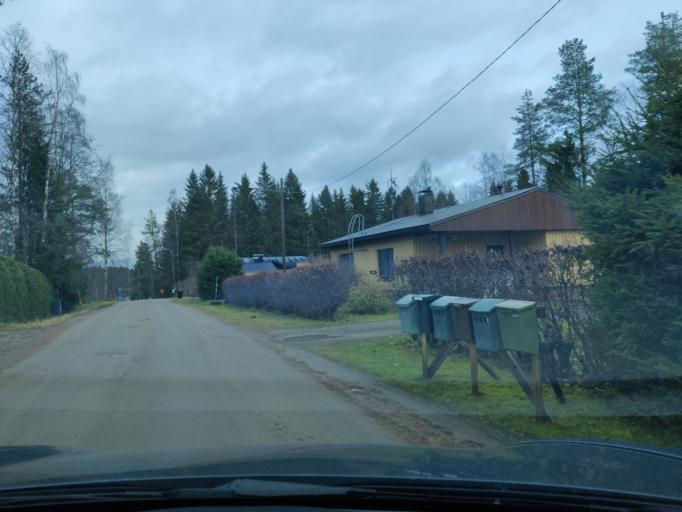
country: FI
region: Northern Savo
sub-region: Ylae-Savo
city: Kiuruvesi
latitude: 63.6457
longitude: 26.6398
